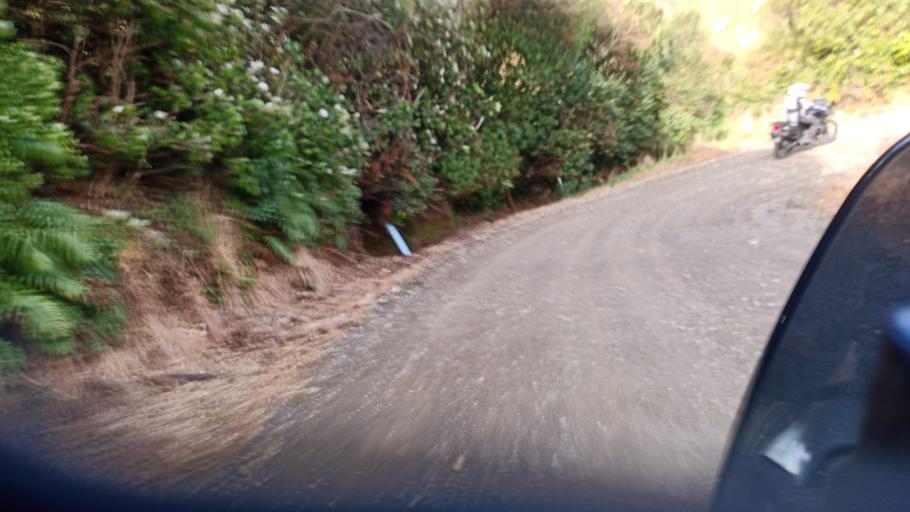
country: NZ
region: Gisborne
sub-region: Gisborne District
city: Gisborne
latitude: -38.4524
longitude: 177.5384
